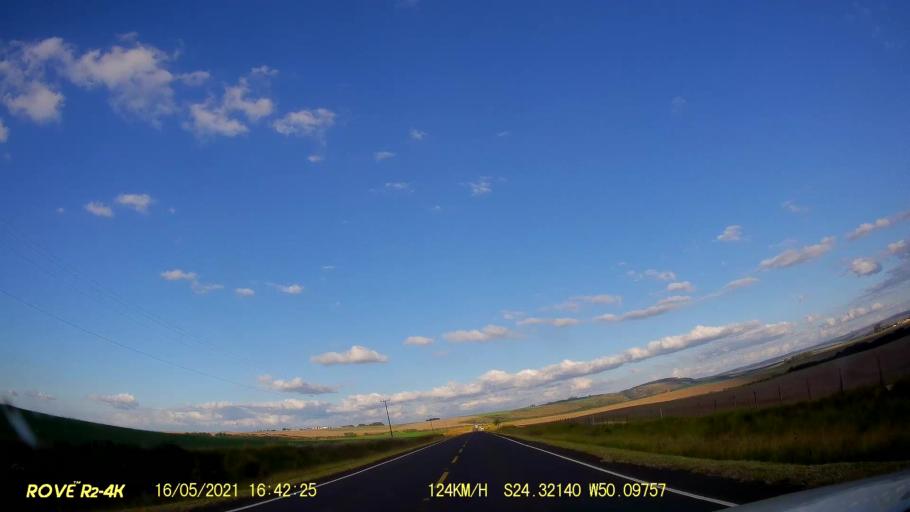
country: BR
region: Parana
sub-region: Pirai Do Sul
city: Pirai do Sul
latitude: -24.3216
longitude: -50.0971
